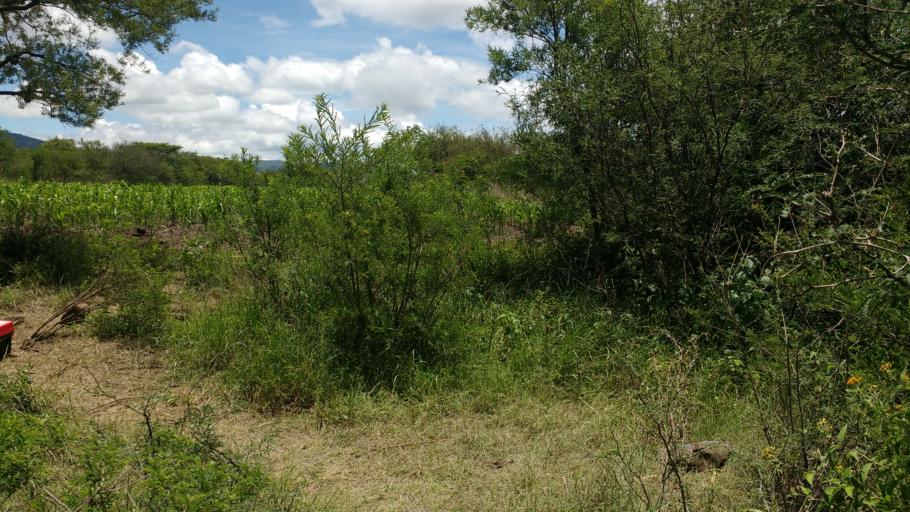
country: MX
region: Hidalgo
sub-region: Tezontepec de Aldama
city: Tenango
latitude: 20.2488
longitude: -99.2750
